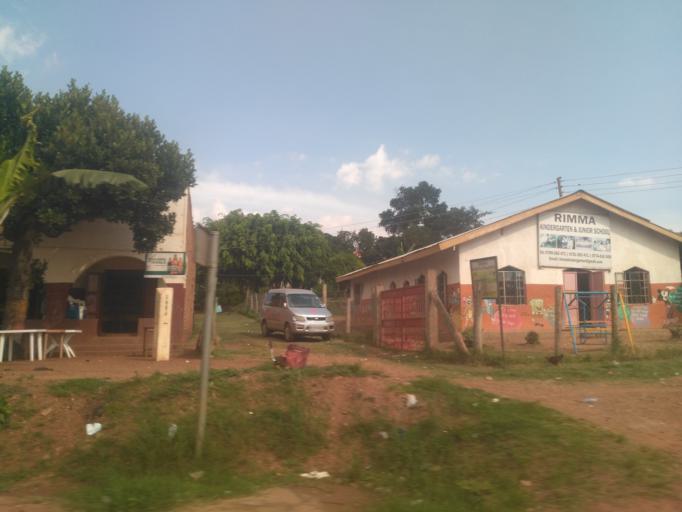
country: UG
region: Central Region
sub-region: Wakiso District
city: Kajansi
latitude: 0.2749
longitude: 32.4678
